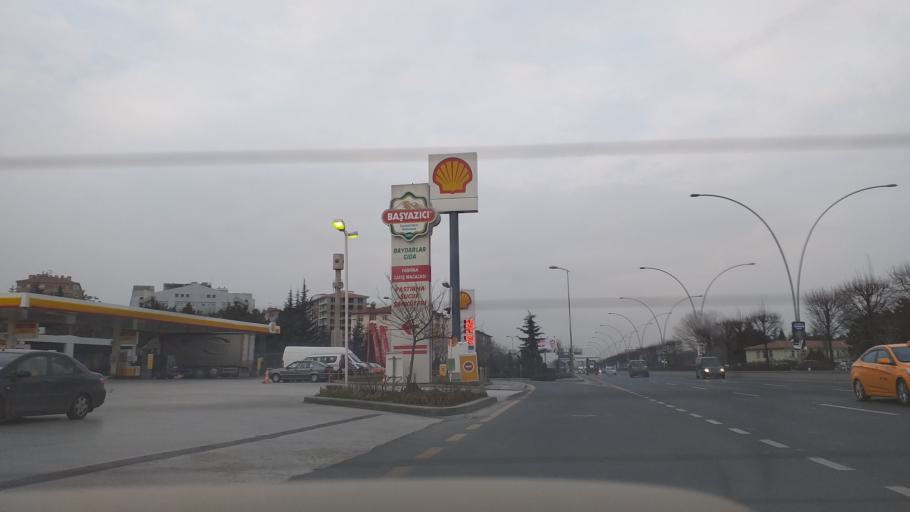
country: TR
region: Ankara
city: Ankara
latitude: 39.9584
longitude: 32.8561
